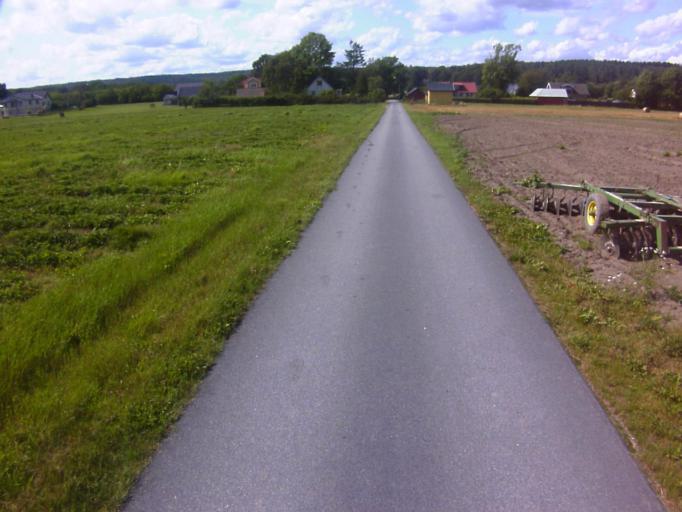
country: SE
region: Blekinge
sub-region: Karlshamns Kommun
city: Morrum
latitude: 56.1647
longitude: 14.6389
